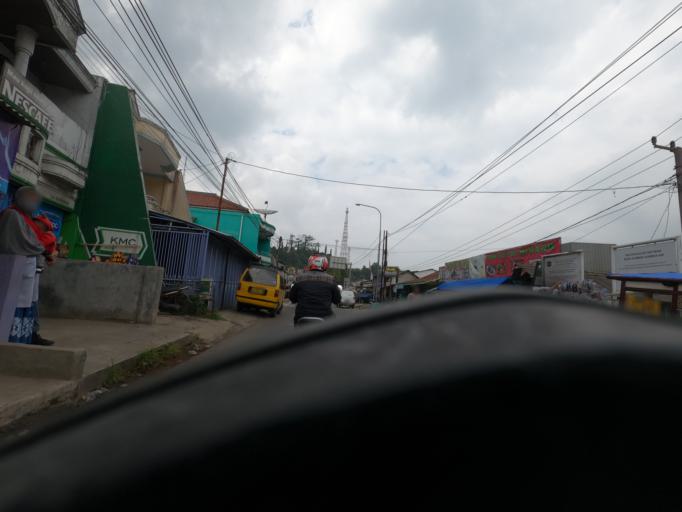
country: ID
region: West Java
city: Lembang
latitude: -6.8112
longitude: 107.5604
